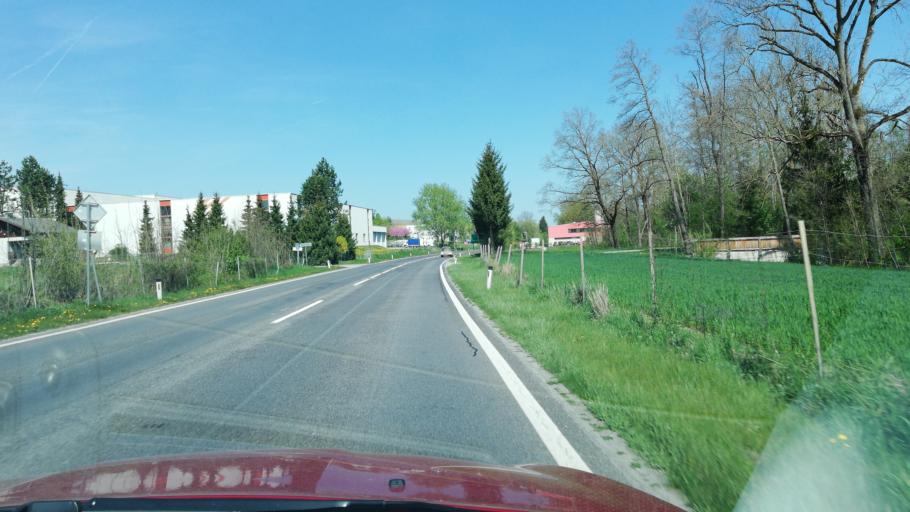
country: AT
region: Upper Austria
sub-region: Wels-Land
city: Thalheim bei Wels
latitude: 48.1358
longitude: 14.0481
